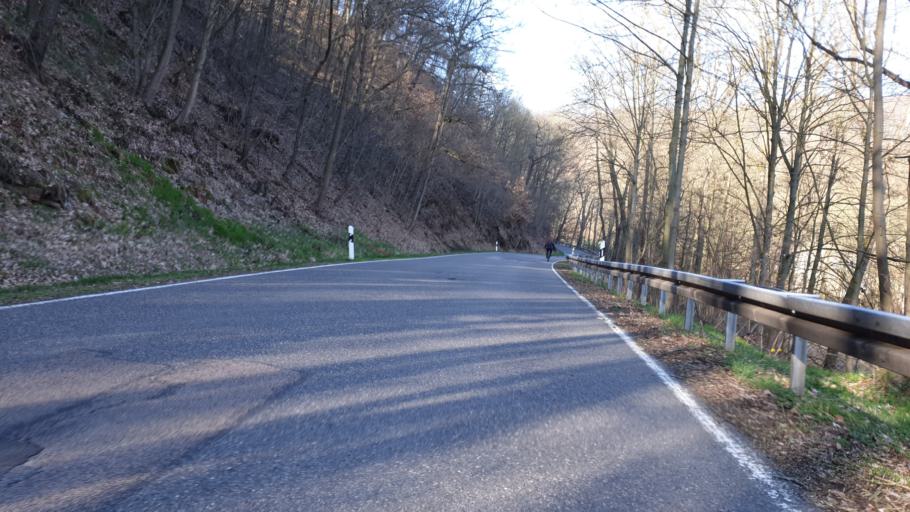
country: DE
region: Saxony
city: Taura
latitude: 50.9403
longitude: 12.8393
